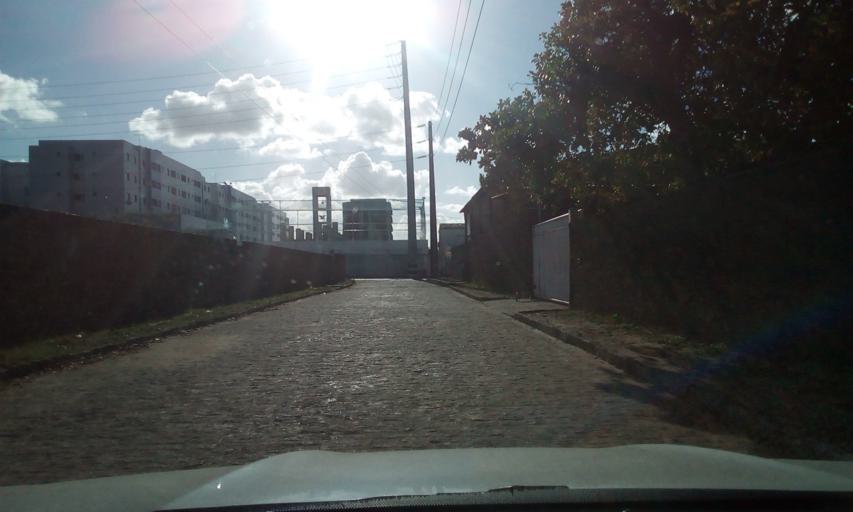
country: BR
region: Paraiba
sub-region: Bayeux
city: Bayeux
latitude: -7.1432
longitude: -34.9078
